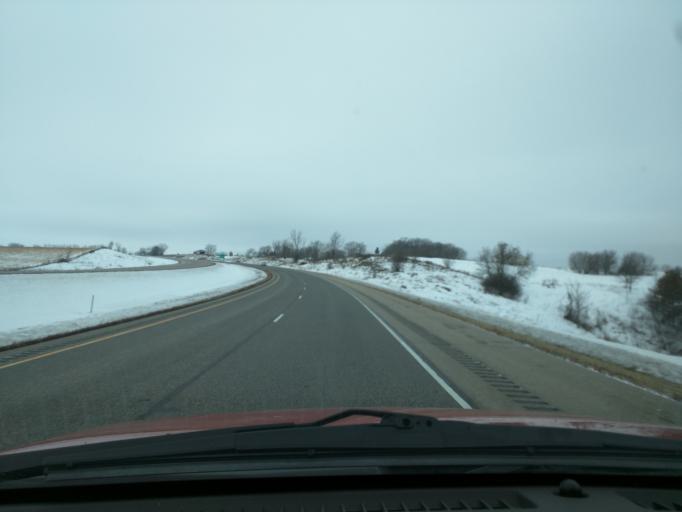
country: US
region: Minnesota
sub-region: Winona County
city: Winona
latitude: 43.9561
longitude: -91.6576
